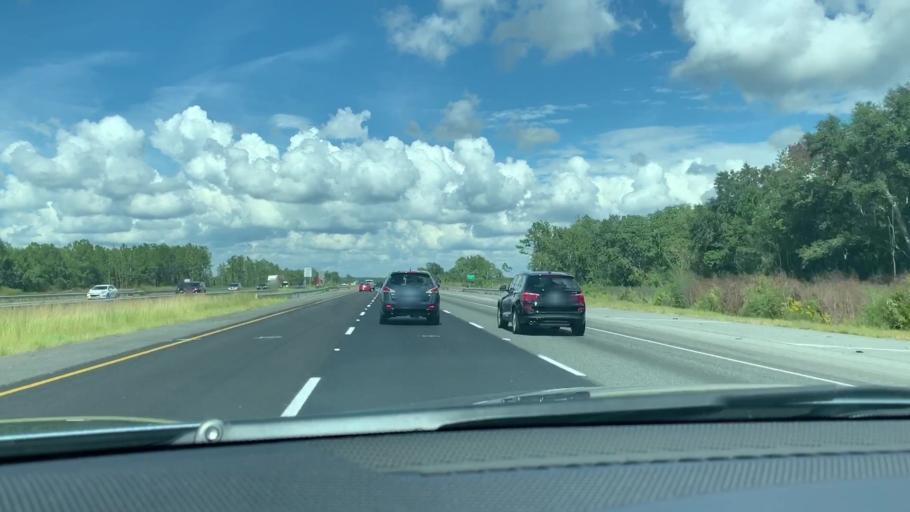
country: US
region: Georgia
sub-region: Camden County
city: Woodbine
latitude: 31.0148
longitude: -81.6592
